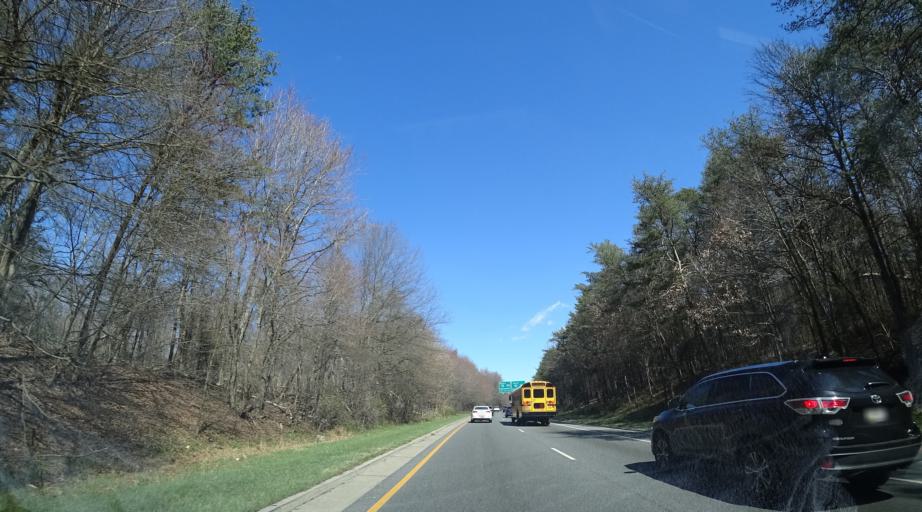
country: US
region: Maryland
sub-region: Prince George's County
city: New Carrollton
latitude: 38.9862
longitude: -76.8906
